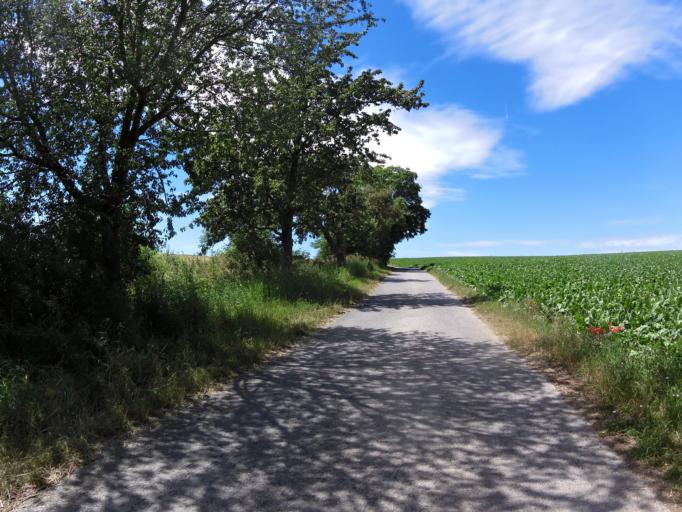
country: DE
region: Bavaria
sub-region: Regierungsbezirk Unterfranken
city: Reichenberg
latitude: 49.7167
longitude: 9.9120
